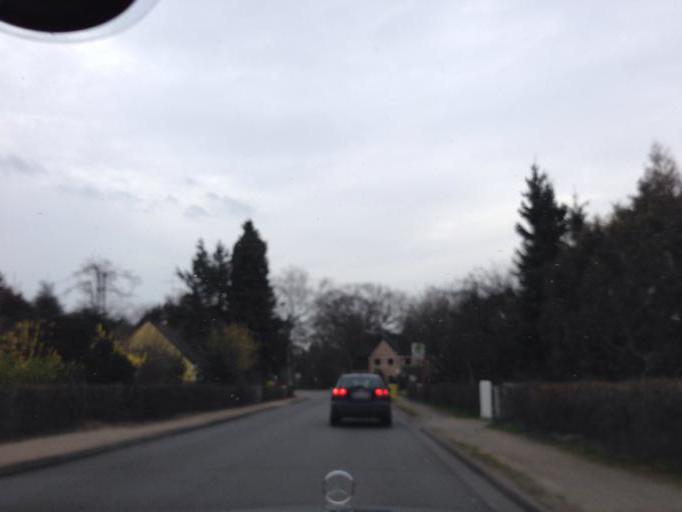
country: DE
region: Hamburg
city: Farmsen-Berne
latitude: 53.6318
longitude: 10.1377
